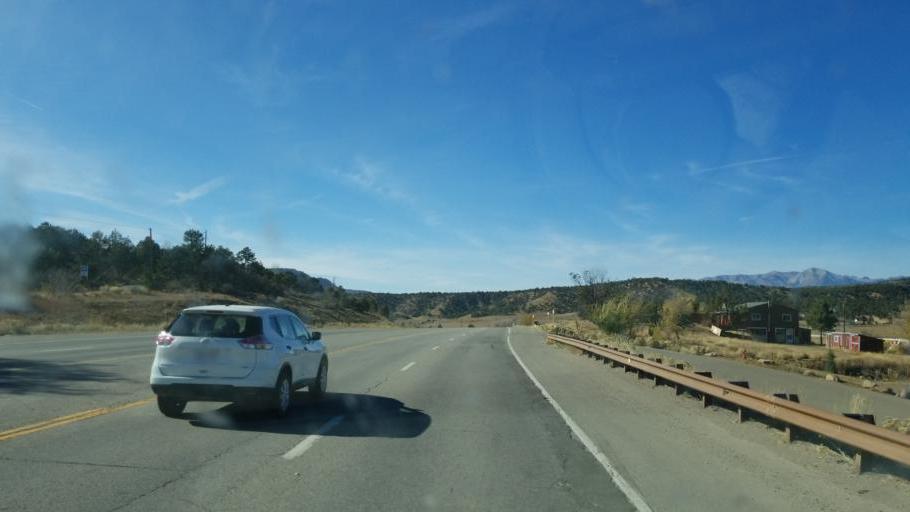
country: US
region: Colorado
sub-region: La Plata County
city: Durango
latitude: 37.2280
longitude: -107.8243
